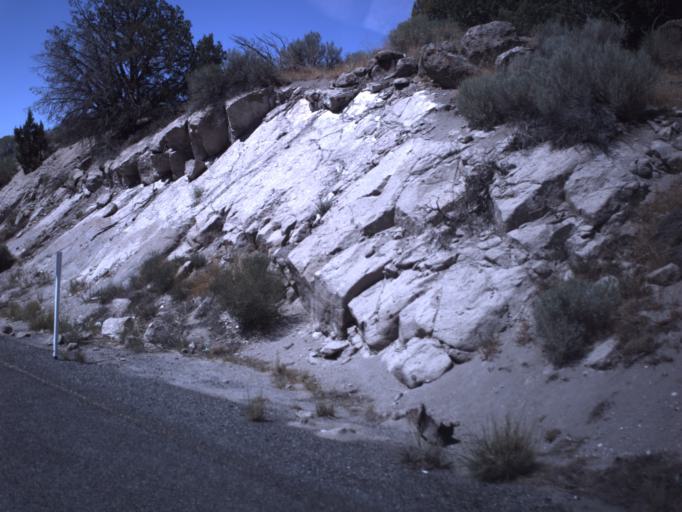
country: US
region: Utah
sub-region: Juab County
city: Nephi
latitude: 39.6415
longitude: -112.0862
